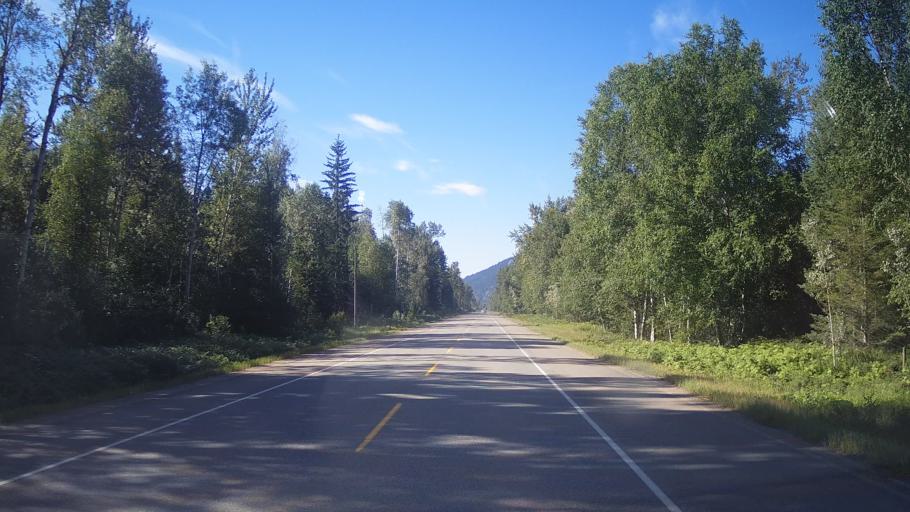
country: CA
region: British Columbia
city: Chase
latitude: 51.5180
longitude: -120.1727
